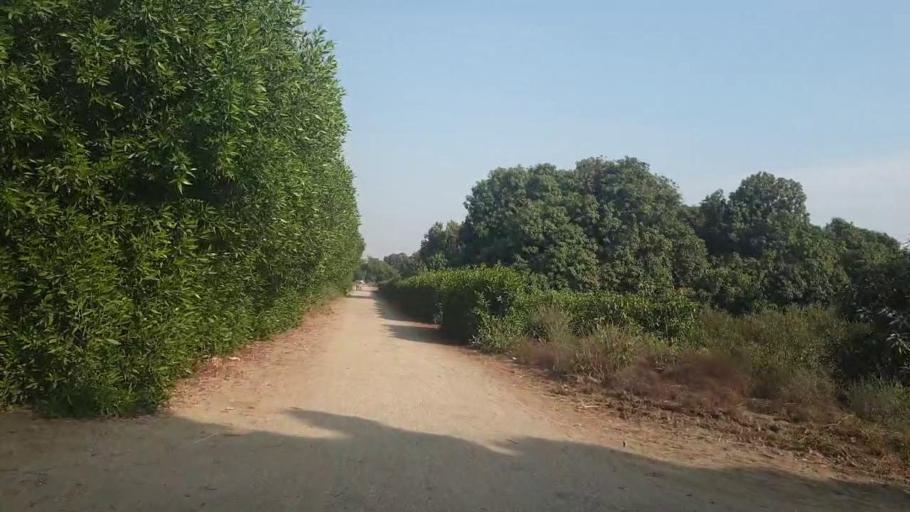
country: PK
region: Sindh
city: Tando Jam
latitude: 25.4295
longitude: 68.4649
